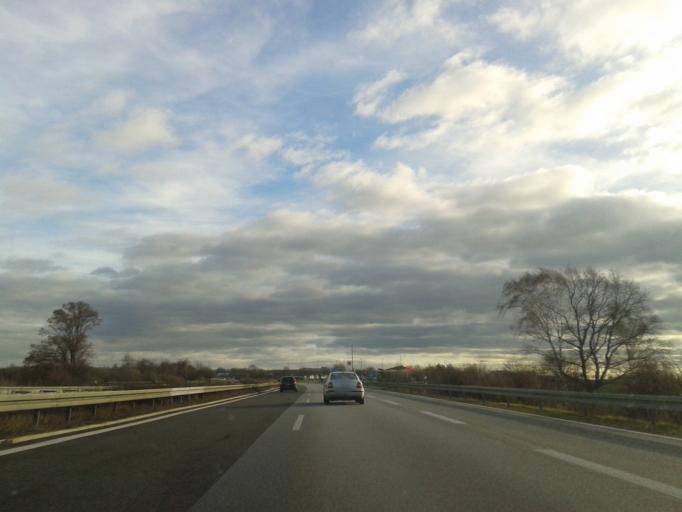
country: DE
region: Saxony
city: Goda
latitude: 51.2006
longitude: 14.3233
